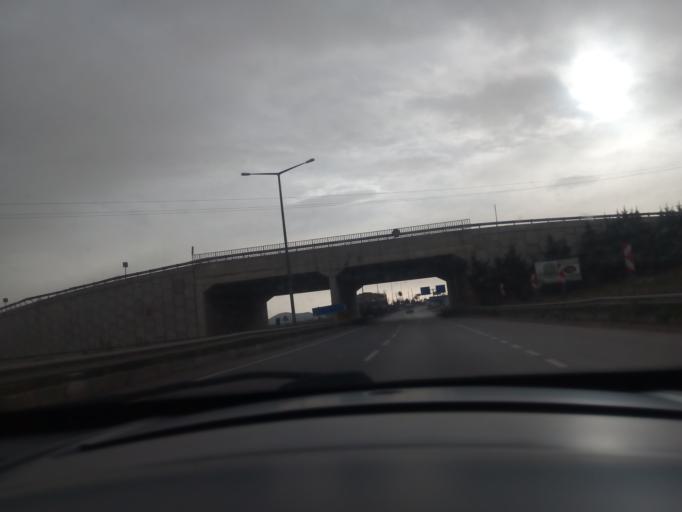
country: TR
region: Bursa
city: Tatkavakli
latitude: 40.0507
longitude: 28.3694
